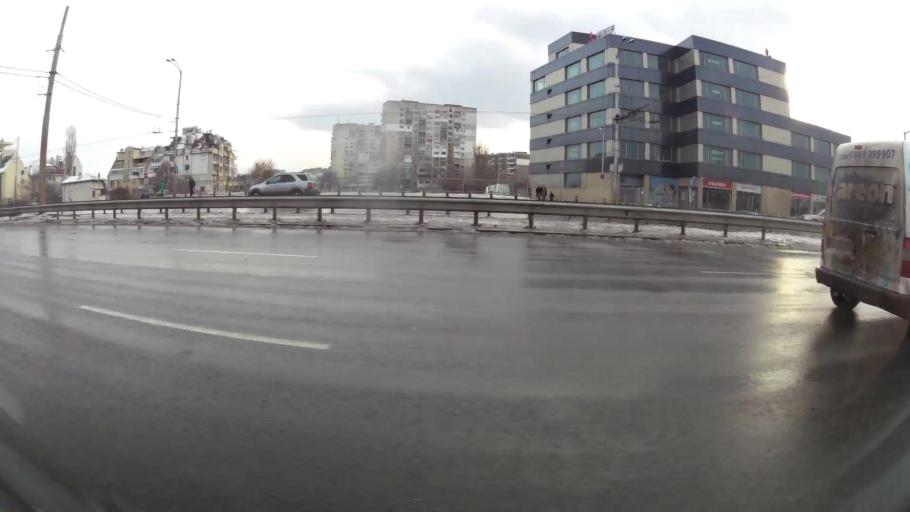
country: BG
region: Sofia-Capital
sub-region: Stolichna Obshtina
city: Sofia
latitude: 42.7087
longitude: 23.3693
